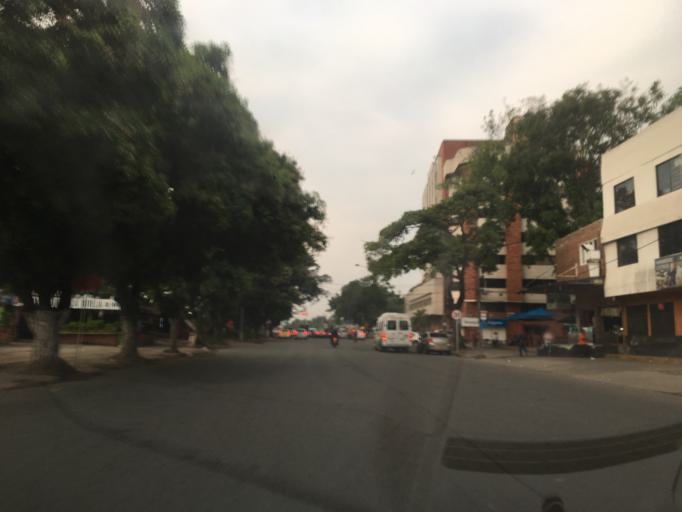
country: CO
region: Valle del Cauca
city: Cali
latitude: 3.4641
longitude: -76.5225
